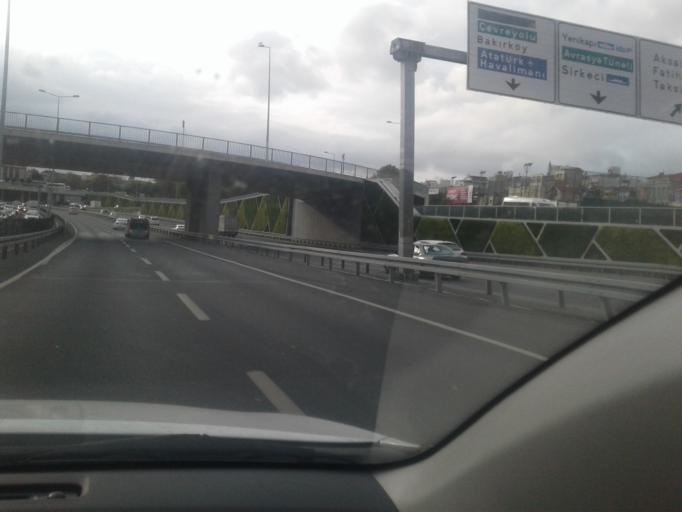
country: TR
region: Istanbul
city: Istanbul
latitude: 41.0037
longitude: 28.9577
